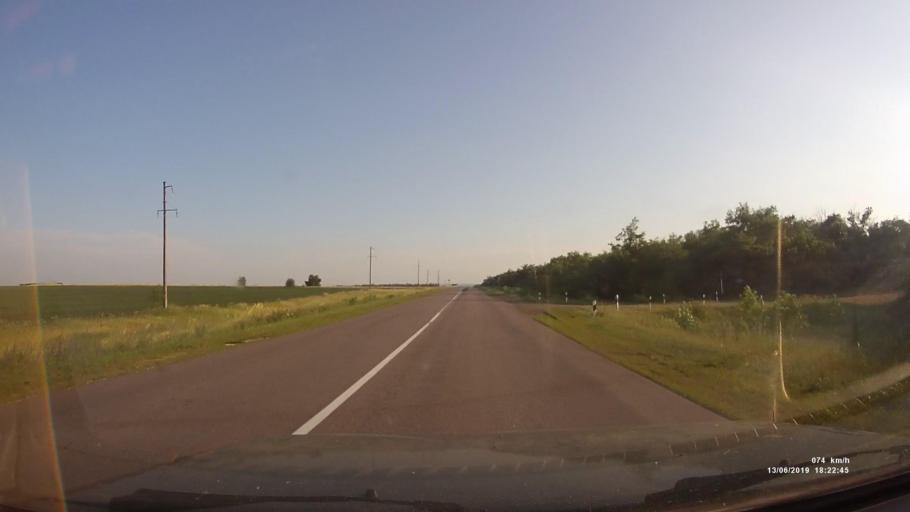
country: RU
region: Rostov
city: Kazanskaya
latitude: 49.8551
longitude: 41.2760
